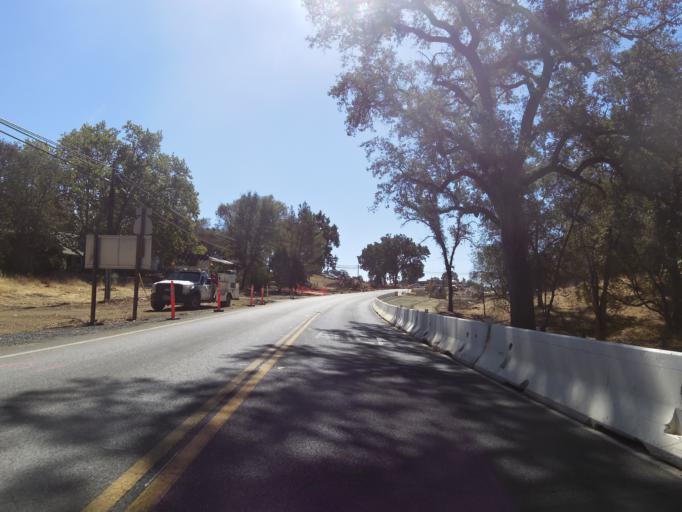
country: US
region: California
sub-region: Amador County
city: Plymouth
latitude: 38.4837
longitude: -120.8451
